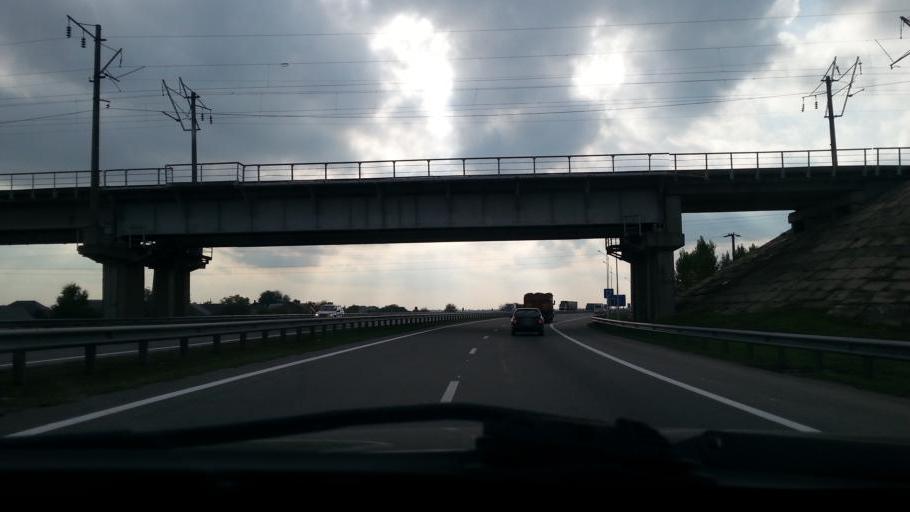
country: RU
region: Rostov
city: Bataysk
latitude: 47.1440
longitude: 39.6993
